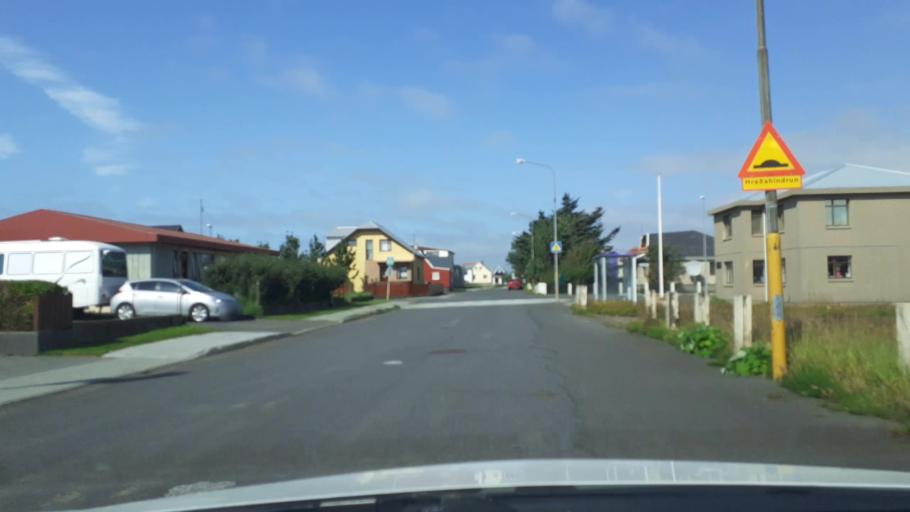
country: IS
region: South
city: Hveragerdi
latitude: 63.8633
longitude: -21.1468
